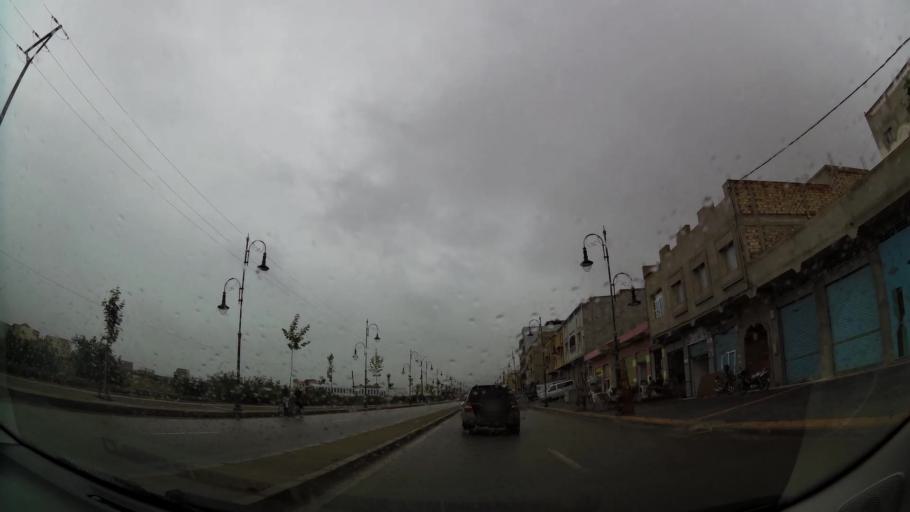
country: MA
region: Taza-Al Hoceima-Taounate
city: Imzourene
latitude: 35.1684
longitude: -3.8583
